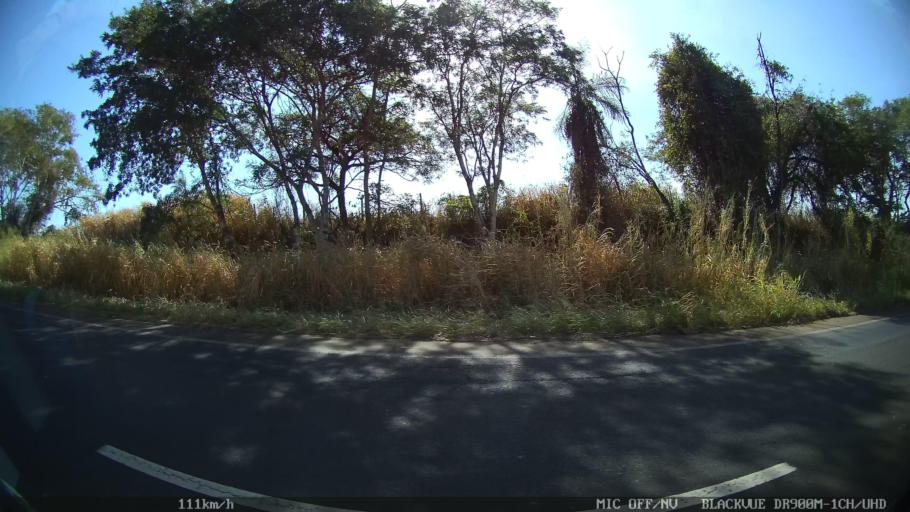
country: BR
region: Sao Paulo
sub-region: Barretos
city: Barretos
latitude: -20.5928
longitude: -48.7120
